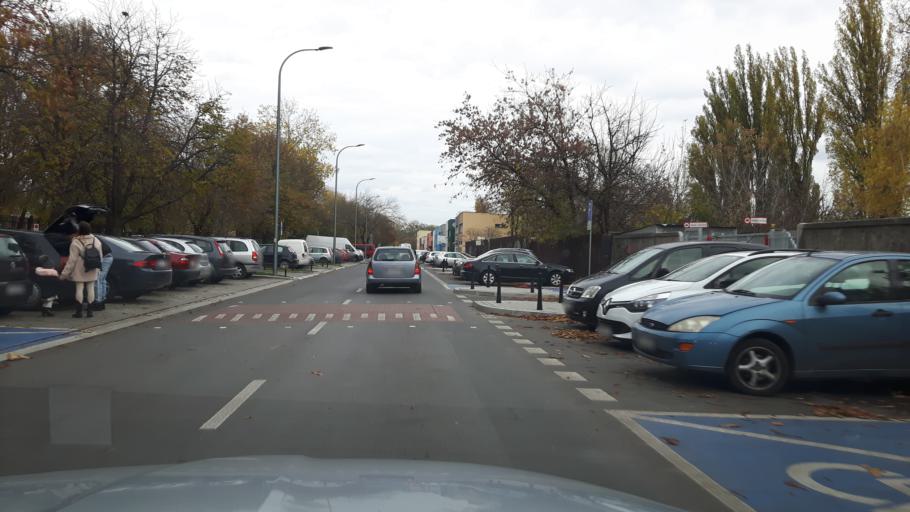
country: PL
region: Masovian Voivodeship
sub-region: Warszawa
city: Mokotow
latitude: 52.1685
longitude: 21.0022
